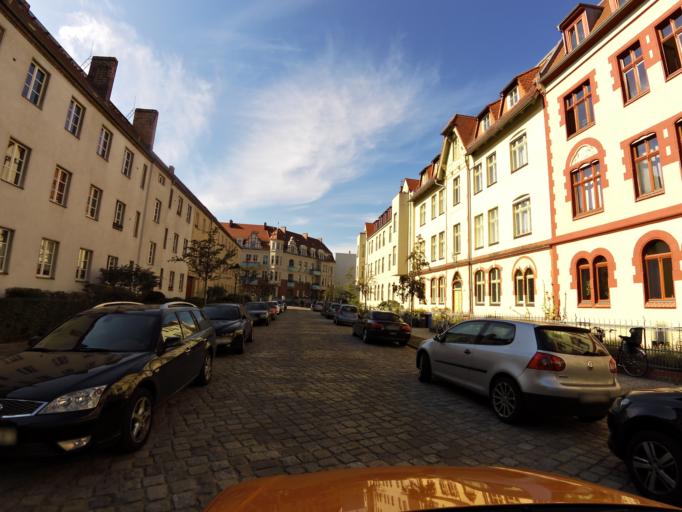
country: DE
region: Brandenburg
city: Potsdam
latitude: 52.3898
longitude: 13.0949
